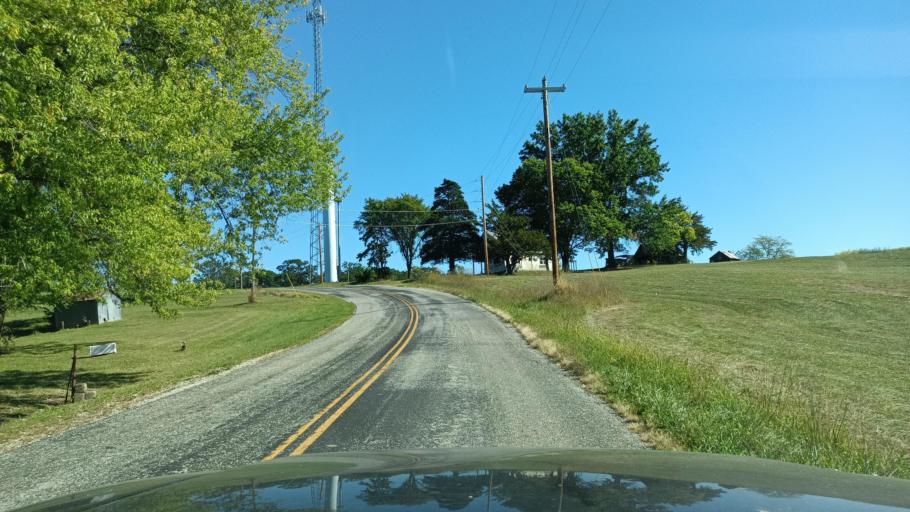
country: US
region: Missouri
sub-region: Macon County
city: La Plata
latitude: 39.9541
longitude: -92.6479
